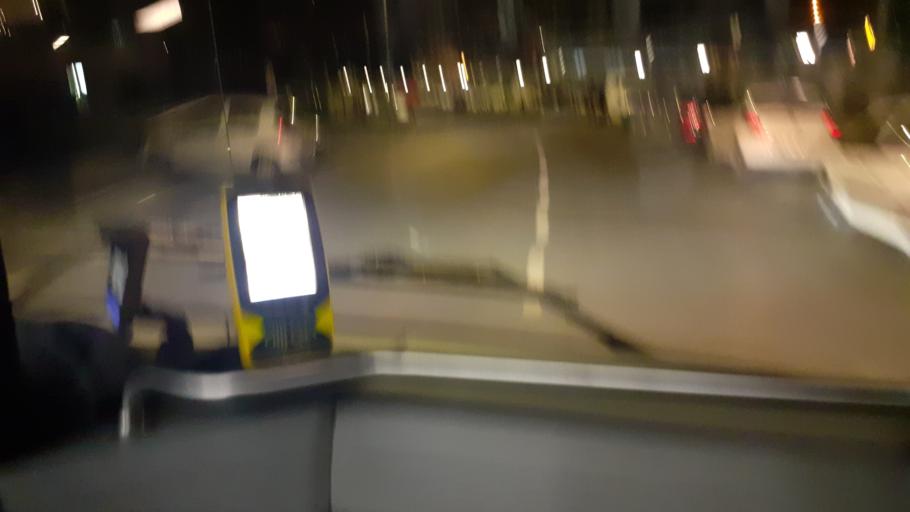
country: TR
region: Istanbul
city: Basaksehir
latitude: 41.0740
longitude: 28.7786
